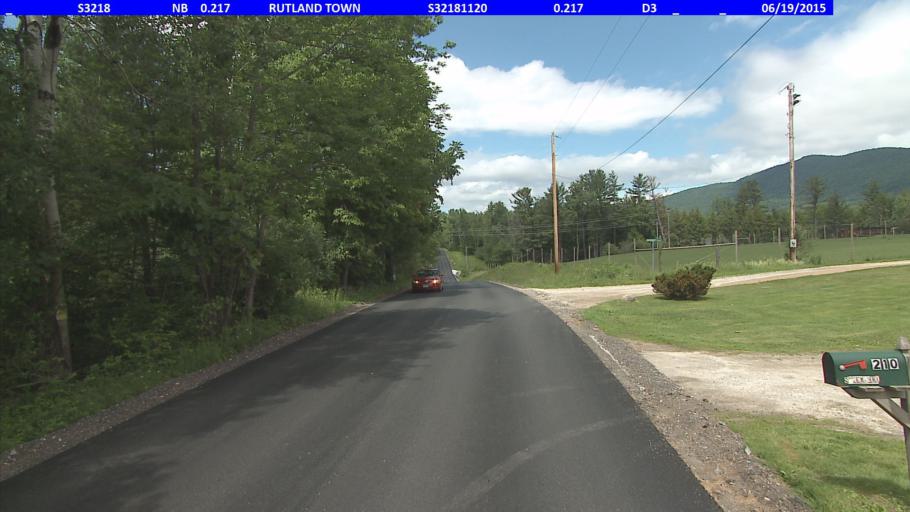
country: US
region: Vermont
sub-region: Rutland County
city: Rutland
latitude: 43.5891
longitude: -72.9510
